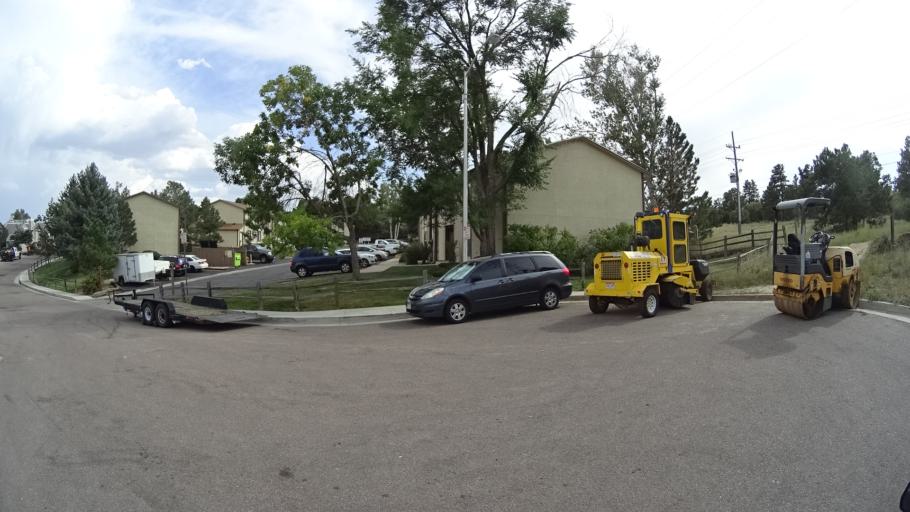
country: US
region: Colorado
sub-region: El Paso County
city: Cimarron Hills
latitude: 38.8780
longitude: -104.7642
